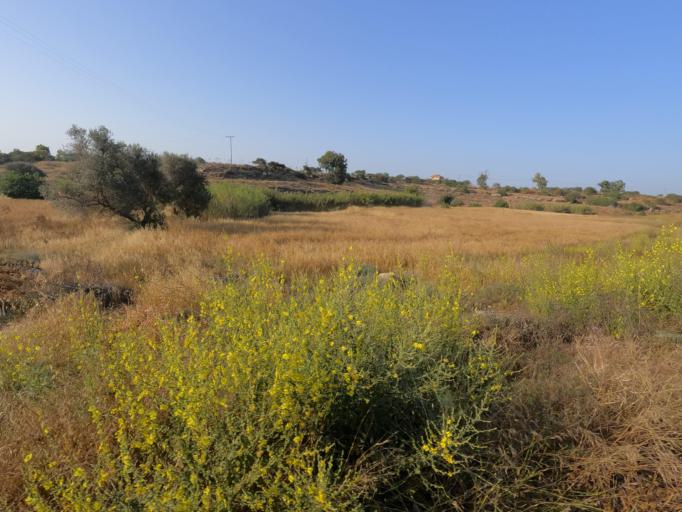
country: CY
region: Ammochostos
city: Liopetri
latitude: 34.9766
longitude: 33.8913
